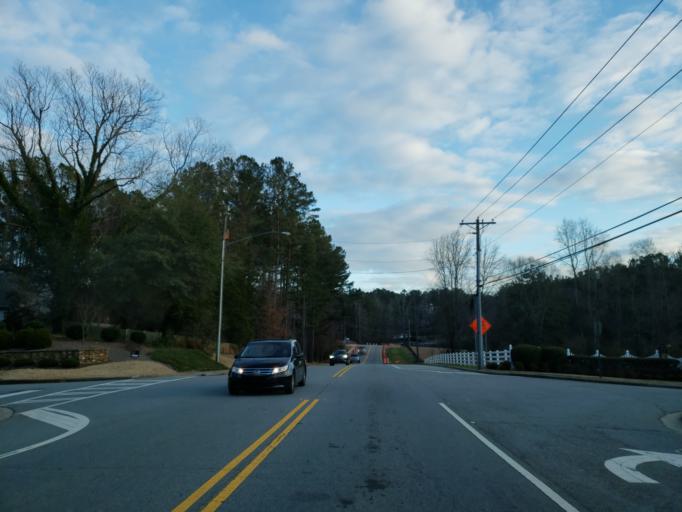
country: US
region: Georgia
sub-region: Cobb County
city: Acworth
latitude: 34.0039
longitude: -84.6775
